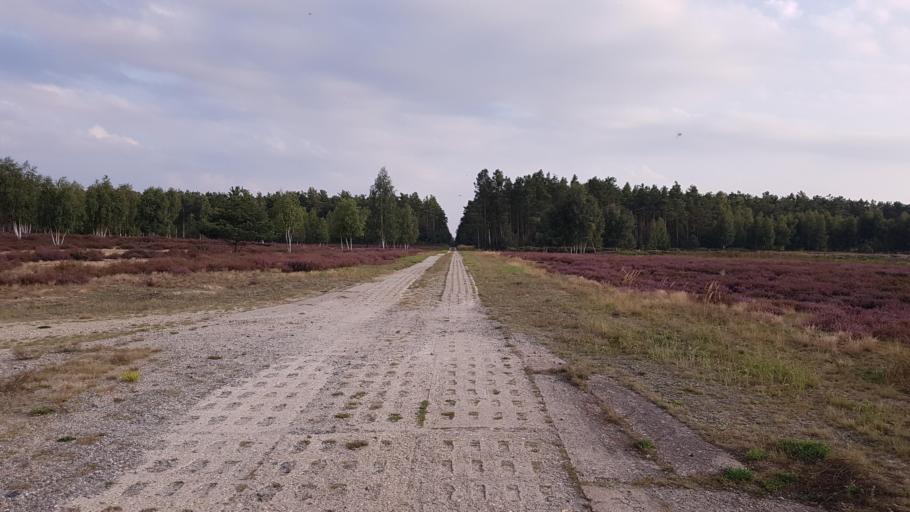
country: DE
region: Brandenburg
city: Schonborn
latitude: 51.6378
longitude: 13.4961
